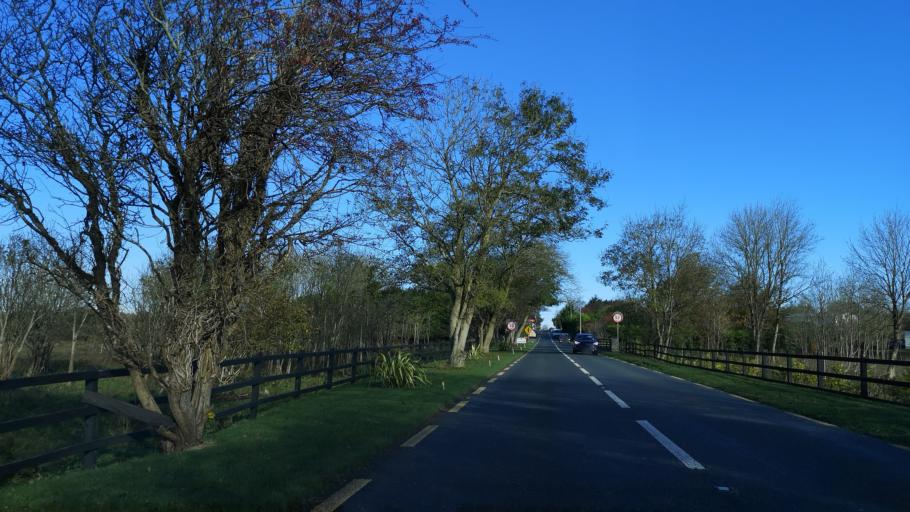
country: IE
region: Connaught
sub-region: County Galway
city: Claregalway
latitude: 53.3721
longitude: -9.0165
